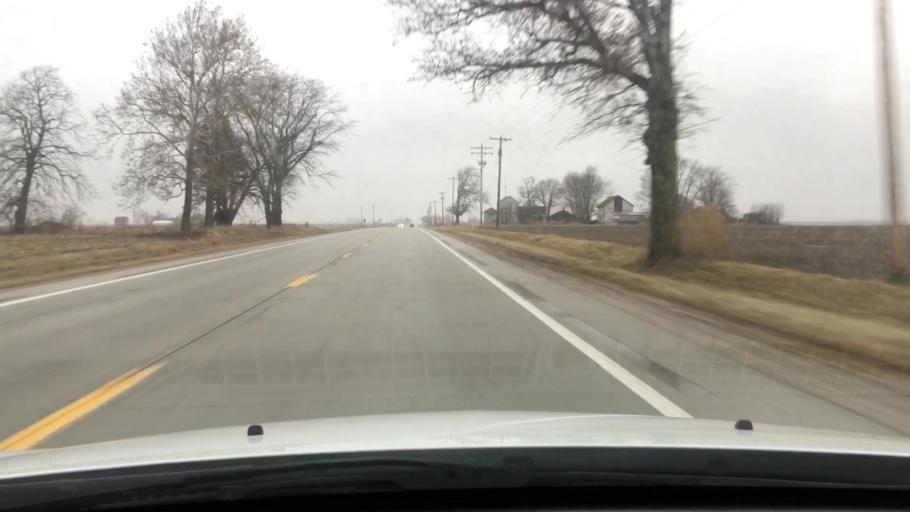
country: US
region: Illinois
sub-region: Livingston County
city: Flanagan
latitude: 40.8721
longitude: -88.7722
